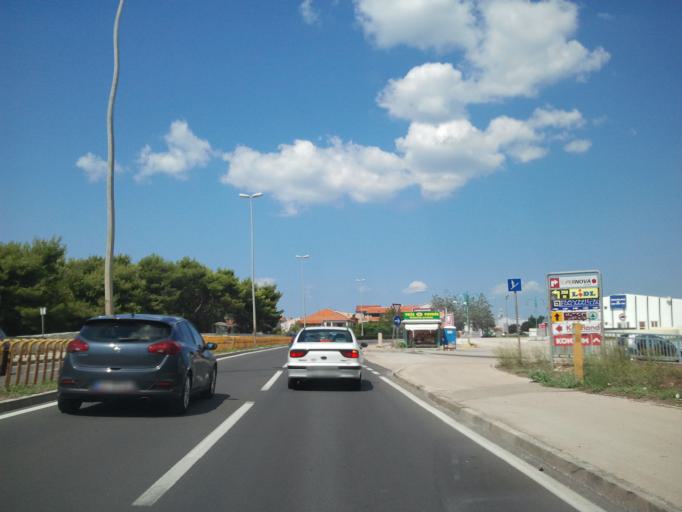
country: HR
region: Zadarska
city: Zadar
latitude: 44.1112
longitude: 15.2563
